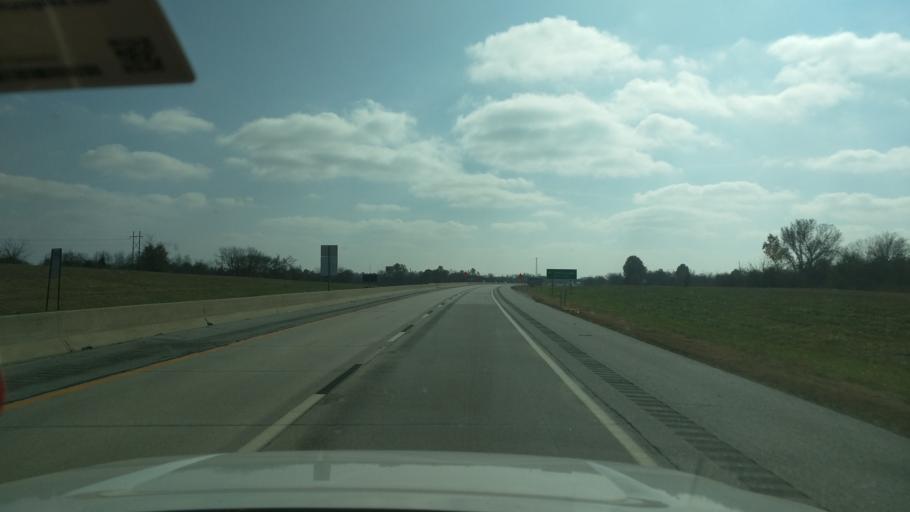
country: US
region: Oklahoma
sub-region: Wagoner County
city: Coweta
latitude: 35.9680
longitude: -95.5942
